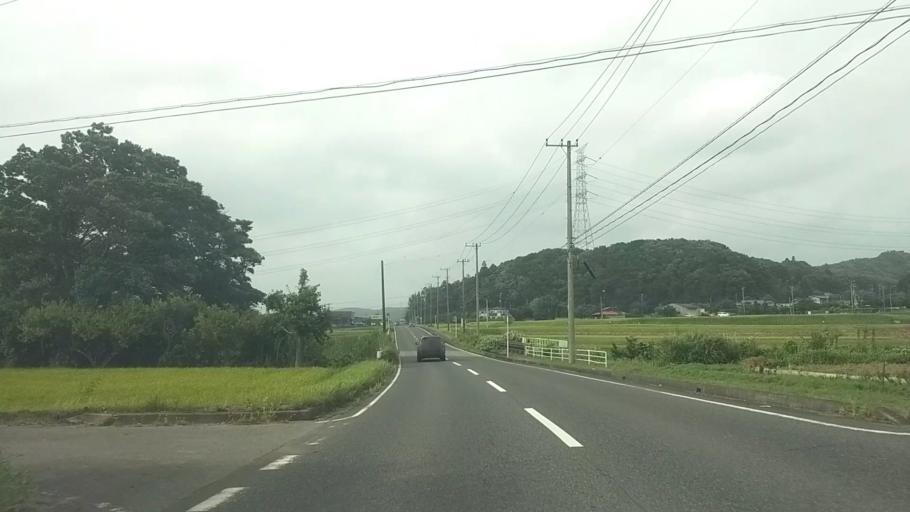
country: JP
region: Chiba
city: Kimitsu
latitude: 35.2803
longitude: 139.9900
